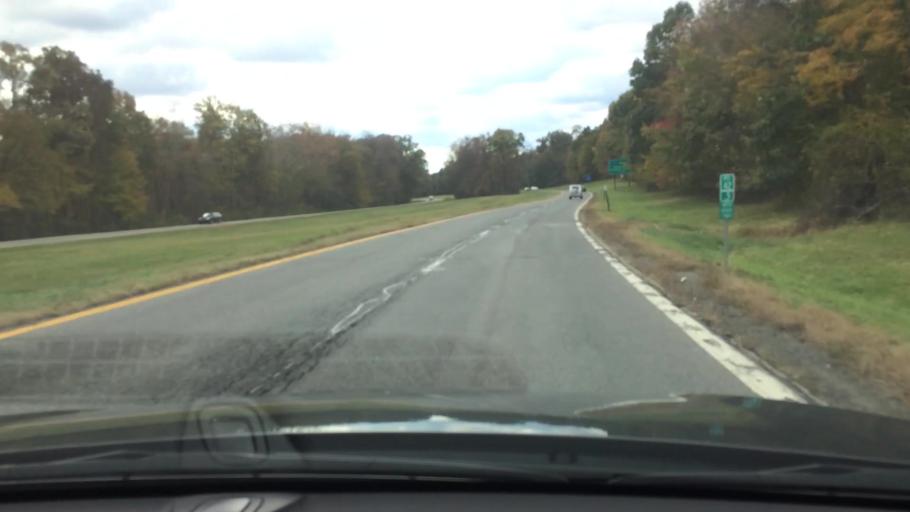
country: US
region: New York
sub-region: Dutchess County
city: Hillside Lake
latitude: 41.6077
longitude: -73.7615
